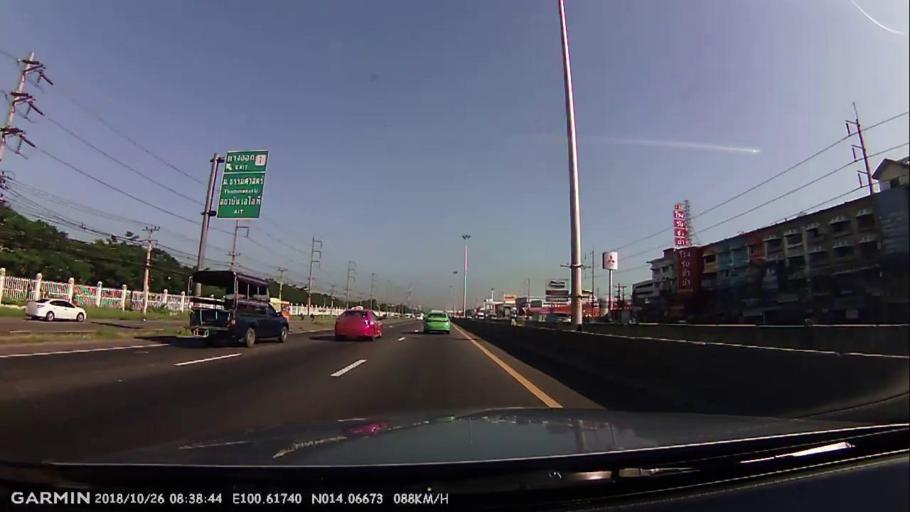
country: TH
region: Pathum Thani
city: Khlong Luang
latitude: 14.0670
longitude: 100.6174
